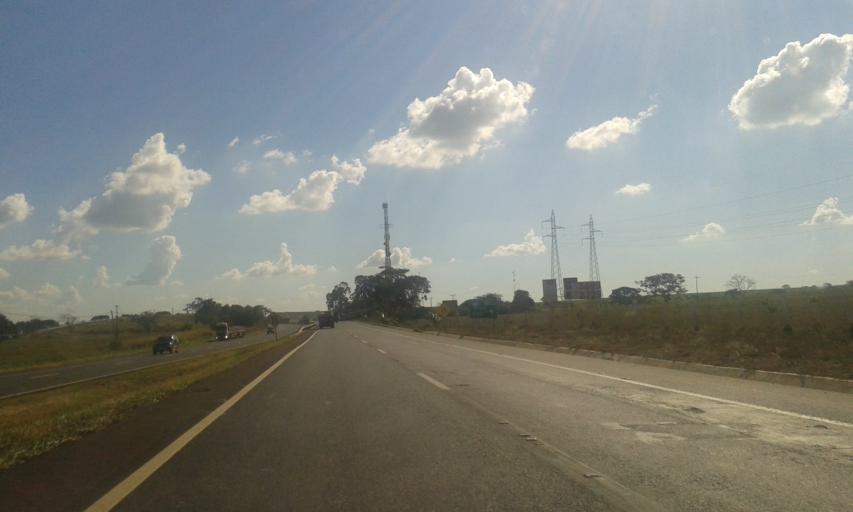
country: BR
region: Minas Gerais
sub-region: Tupaciguara
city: Tupaciguara
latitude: -18.8650
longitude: -48.5808
